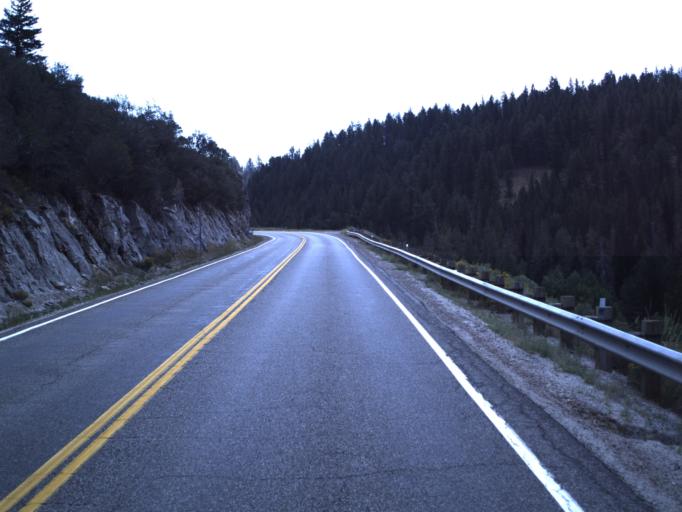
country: US
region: Idaho
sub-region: Bear Lake County
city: Paris
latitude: 41.9599
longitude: -111.5186
